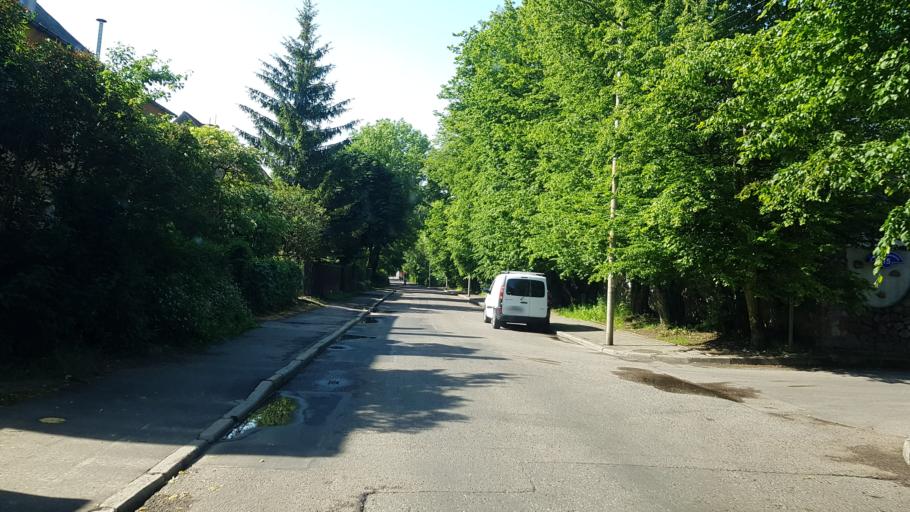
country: RU
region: Kaliningrad
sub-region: Gorod Kaliningrad
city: Kaliningrad
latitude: 54.7164
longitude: 20.4569
